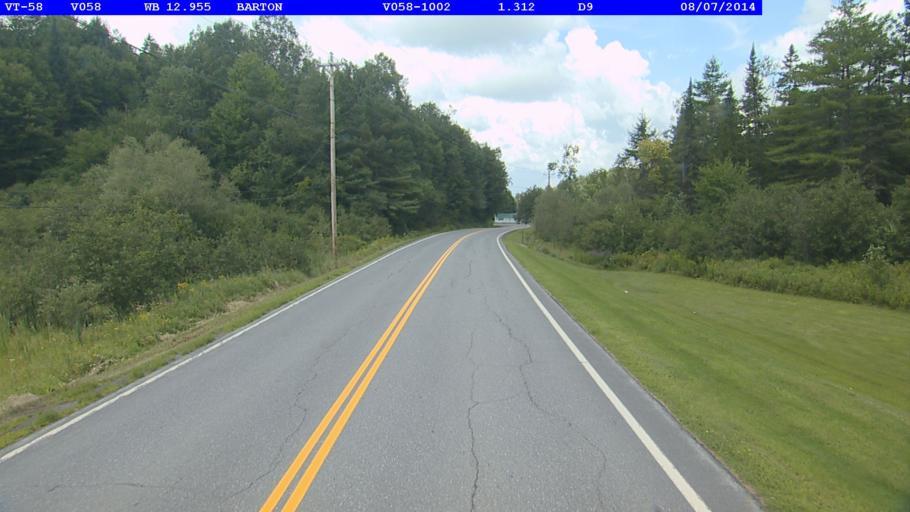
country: US
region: Vermont
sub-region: Orleans County
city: Newport
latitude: 44.8057
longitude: -72.1859
